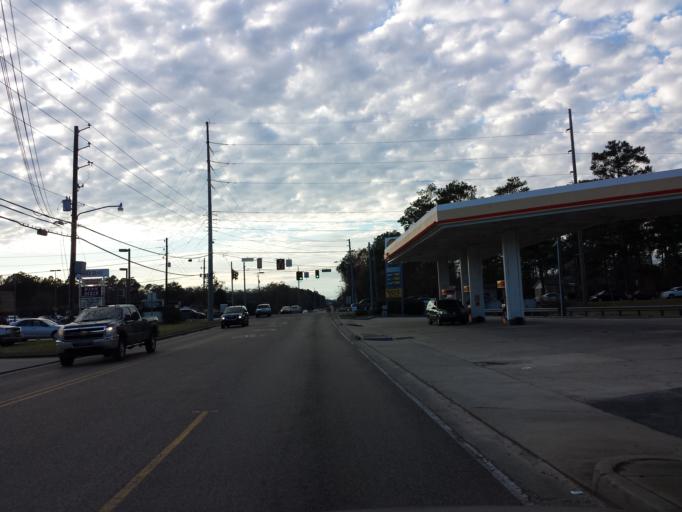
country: US
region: Mississippi
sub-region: Forrest County
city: Hattiesburg
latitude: 31.3041
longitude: -89.3303
